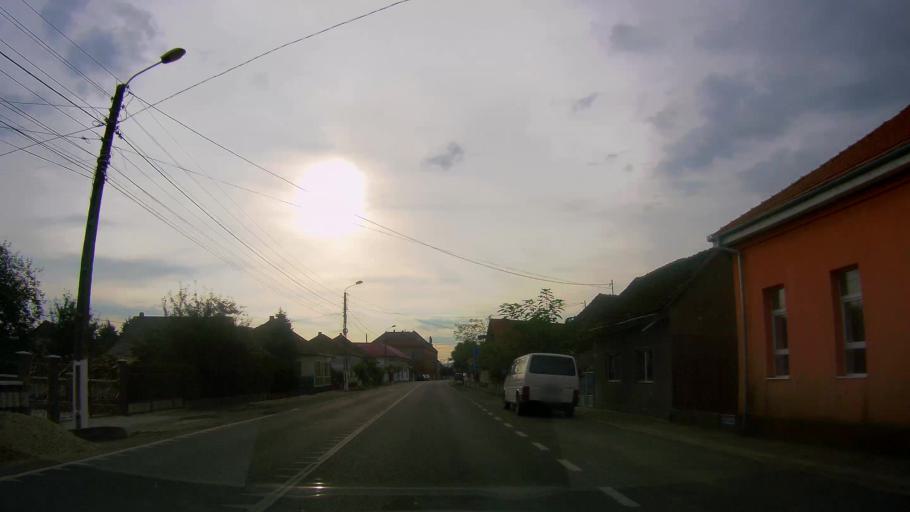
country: RO
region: Satu Mare
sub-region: Comuna Halmeu
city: Halmeu
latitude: 47.9767
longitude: 23.0235
